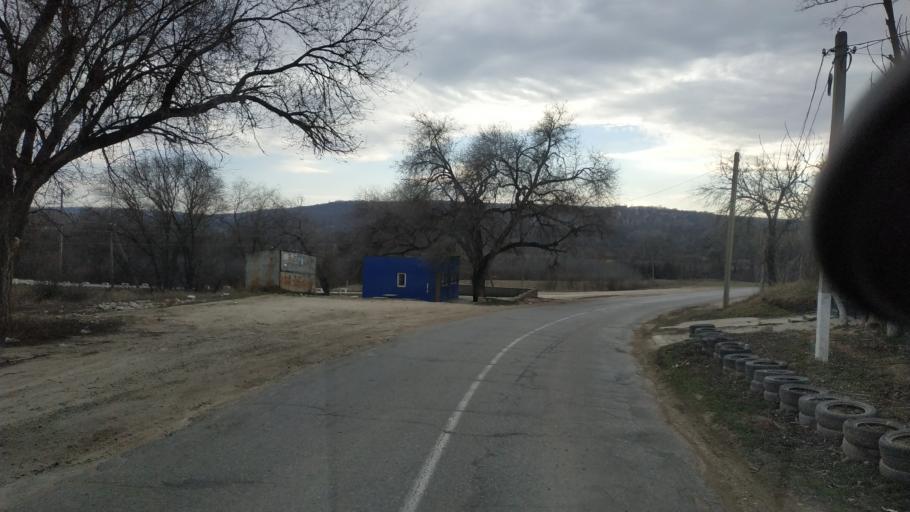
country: MD
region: Chisinau
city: Vadul lui Voda
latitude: 47.1186
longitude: 29.0634
